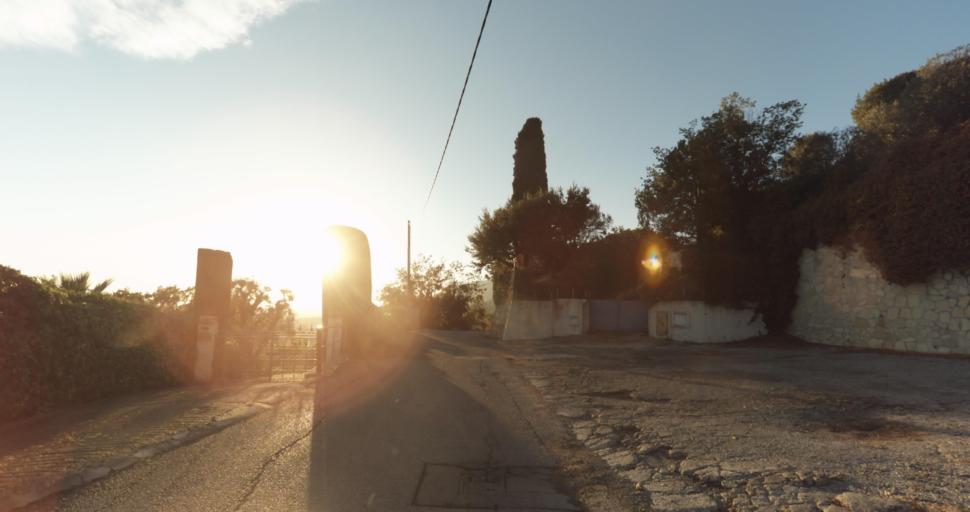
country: FR
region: Provence-Alpes-Cote d'Azur
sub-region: Departement des Alpes-Maritimes
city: Vence
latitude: 43.7288
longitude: 7.0994
